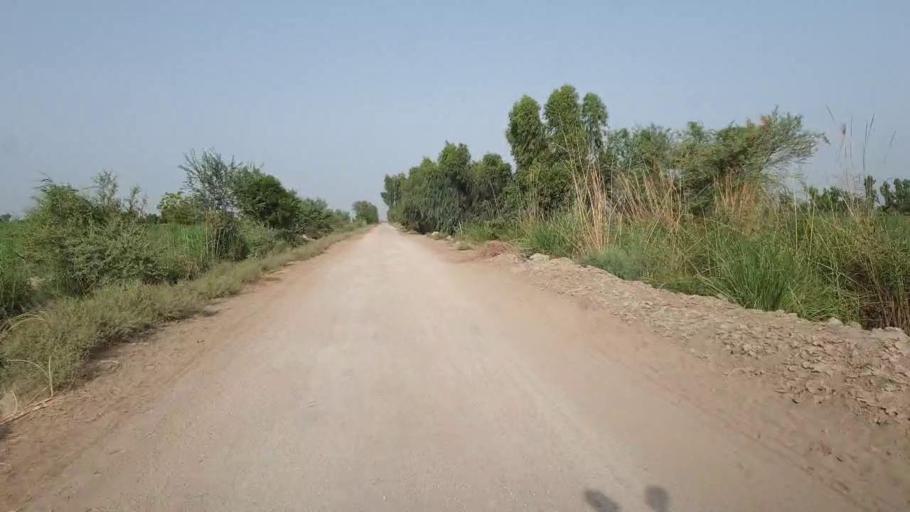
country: PK
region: Sindh
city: Daur
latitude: 26.3407
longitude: 68.1982
